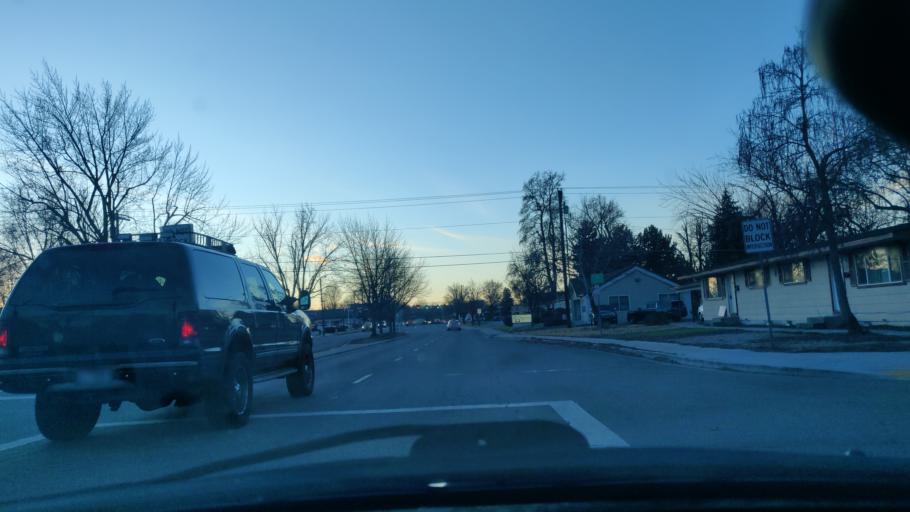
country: US
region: Idaho
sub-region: Ada County
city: Boise
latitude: 43.5986
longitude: -116.1910
